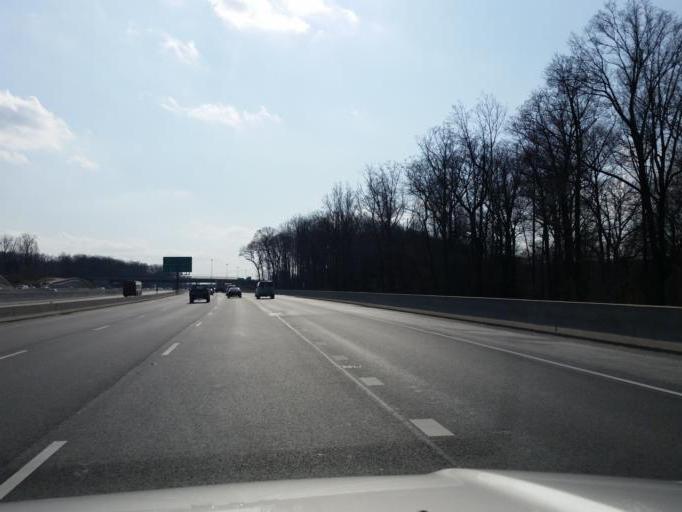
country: US
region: Maryland
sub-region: Baltimore County
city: Rossville
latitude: 39.3630
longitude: -76.4752
